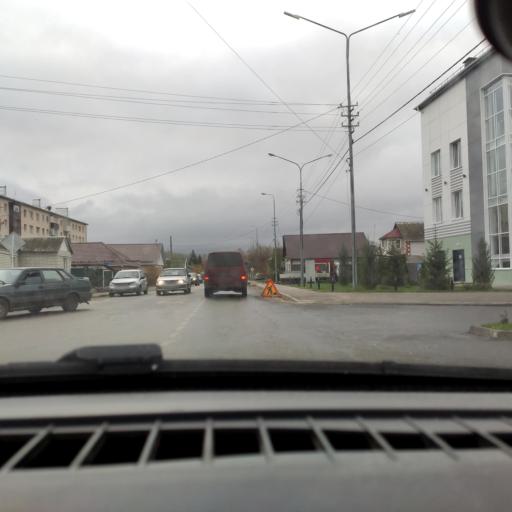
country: RU
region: Belgorod
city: Alekseyevka
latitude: 50.6270
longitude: 38.6899
